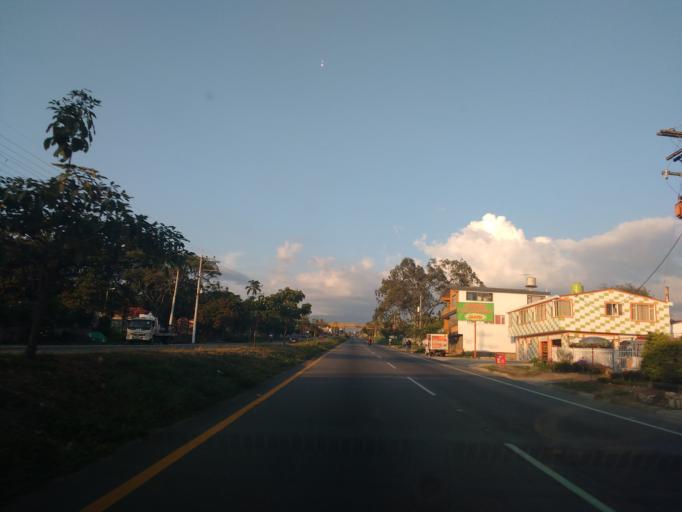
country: CO
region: Cundinamarca
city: Arbelaez
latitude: 4.3100
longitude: -74.4402
